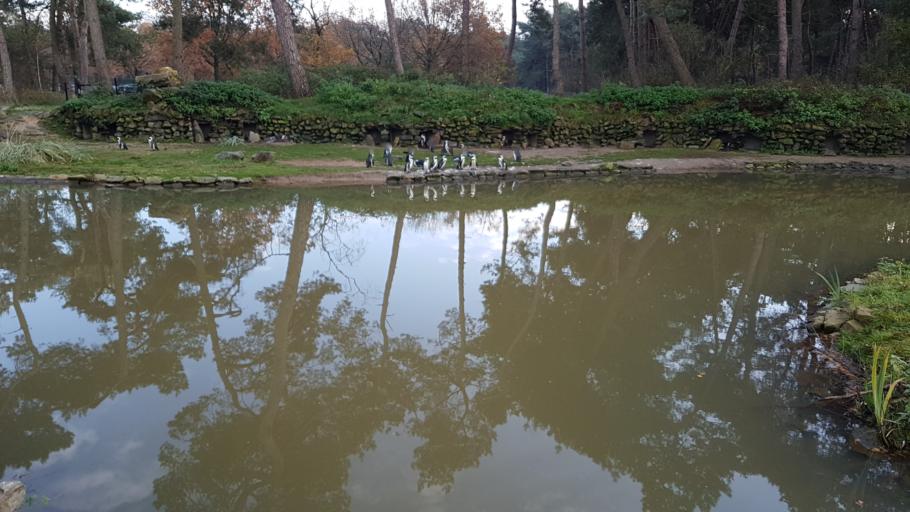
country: NL
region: North Brabant
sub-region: Gemeente Goirle
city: Goirle
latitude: 51.5159
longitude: 5.1007
